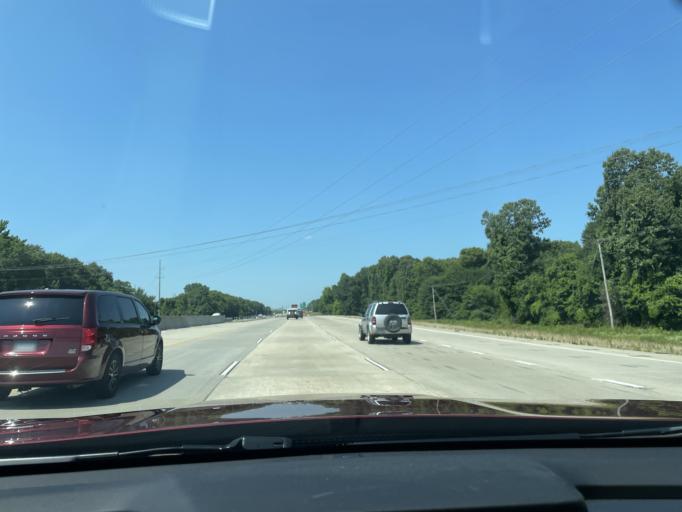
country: US
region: Arkansas
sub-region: Pulaski County
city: Jacksonville
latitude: 34.8571
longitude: -92.1336
